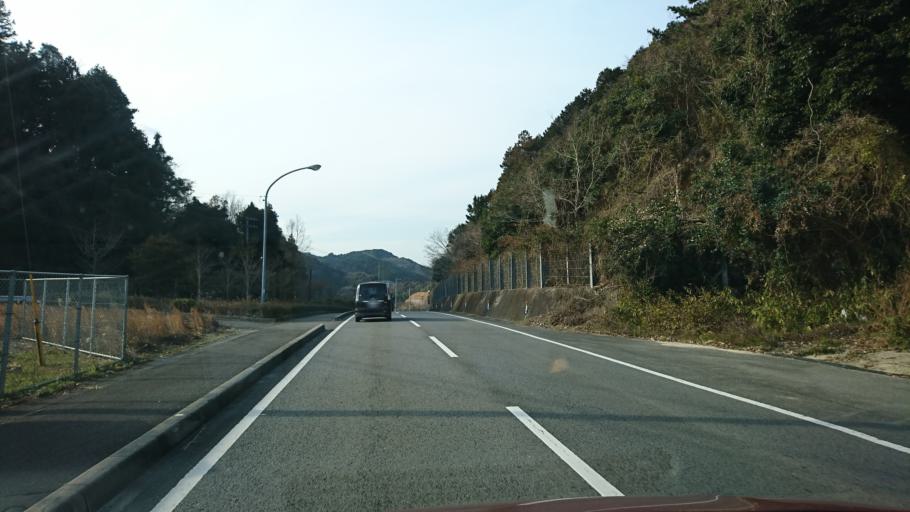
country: JP
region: Ehime
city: Hojo
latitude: 33.9947
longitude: 132.9272
